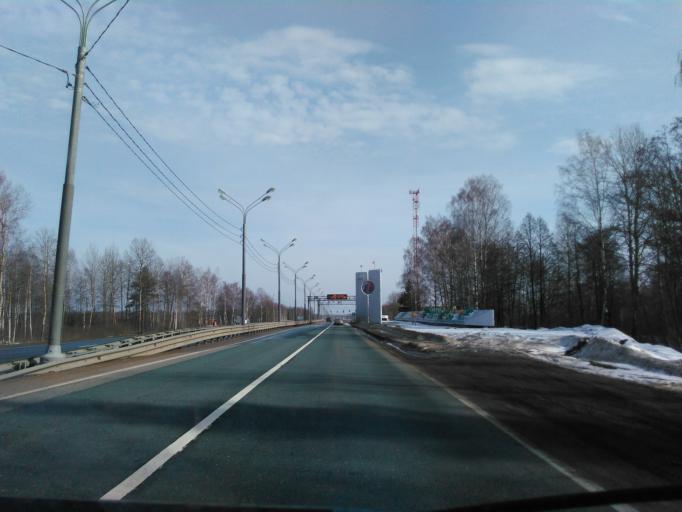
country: RU
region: Smolensk
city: Rudnya
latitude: 54.6907
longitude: 30.9863
